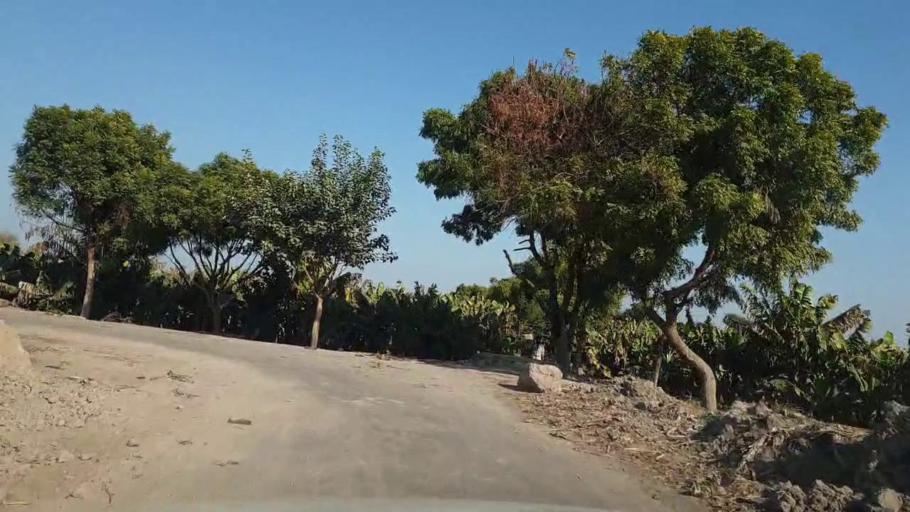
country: PK
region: Sindh
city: Tando Allahyar
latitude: 25.4790
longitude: 68.6600
